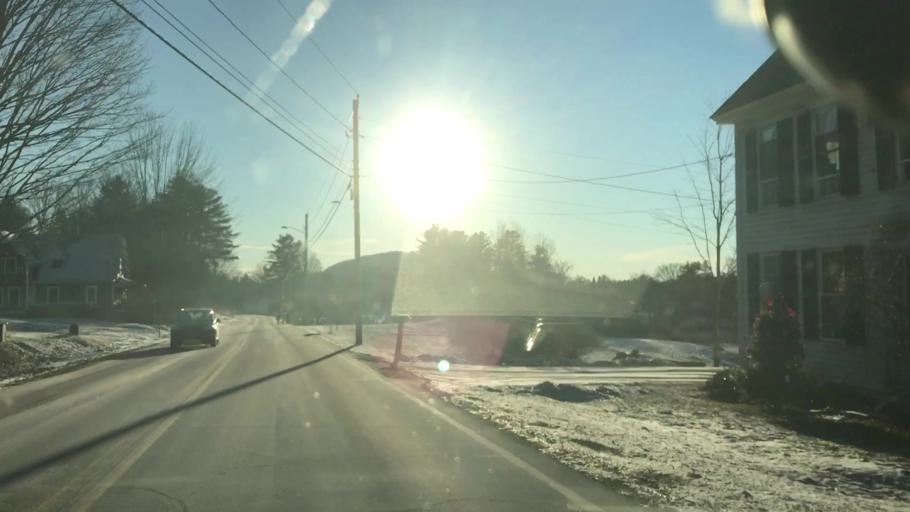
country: US
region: New Hampshire
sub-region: Grafton County
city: Lyme Town Offices
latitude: 43.8137
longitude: -72.1529
